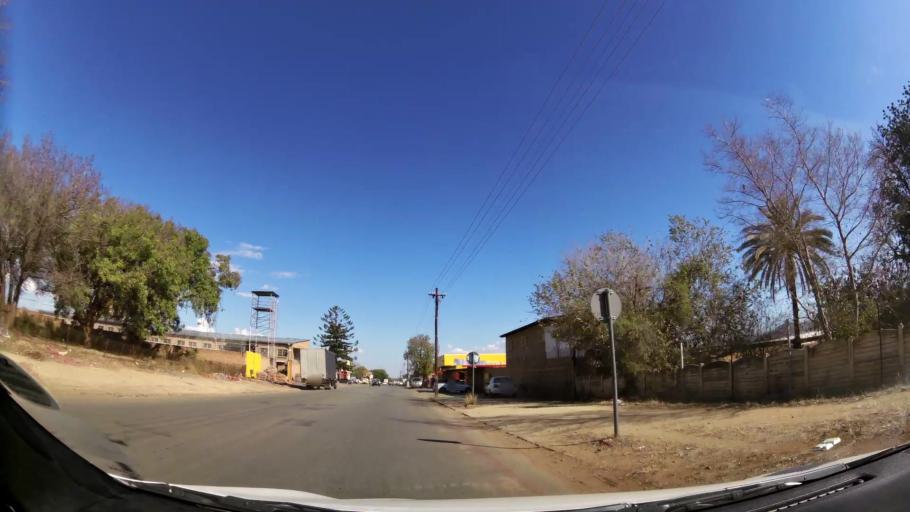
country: ZA
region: Limpopo
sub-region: Waterberg District Municipality
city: Mokopane
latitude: -24.1790
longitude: 29.0167
